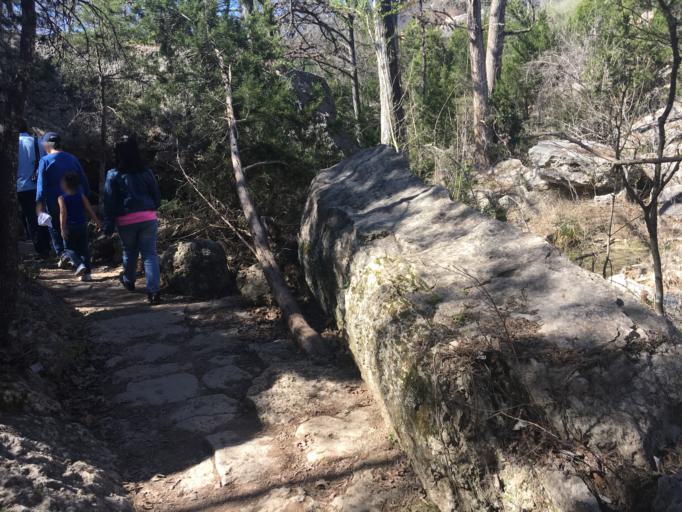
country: US
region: Texas
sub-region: Travis County
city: Briarcliff
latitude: 30.3430
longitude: -98.1282
